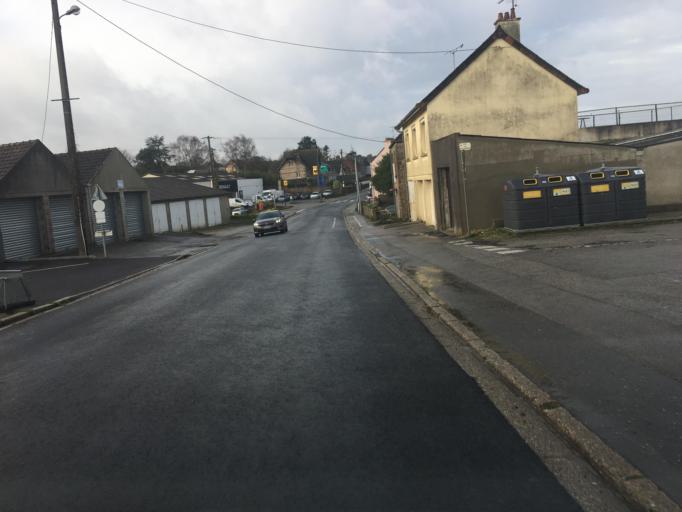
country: FR
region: Lower Normandy
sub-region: Departement de la Manche
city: Saint-Pierre-Eglise
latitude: 49.6669
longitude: -1.3973
